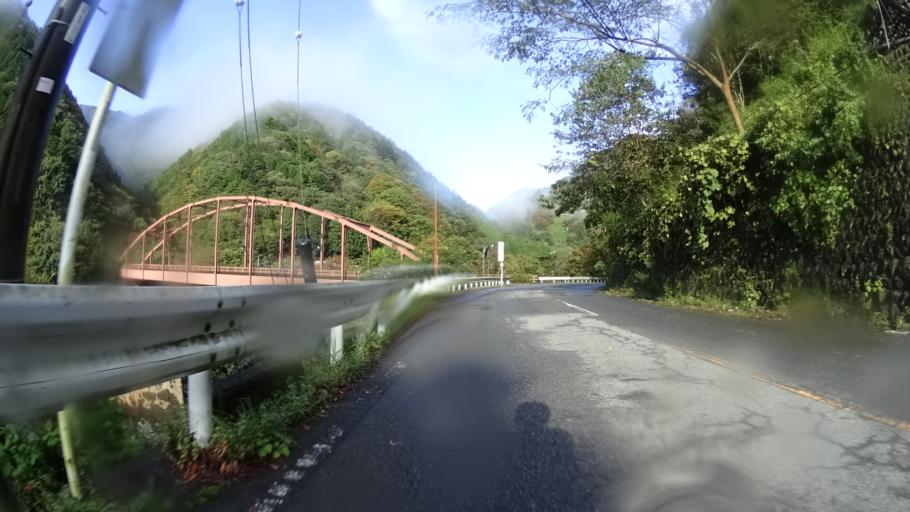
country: JP
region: Yamanashi
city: Otsuki
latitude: 35.7795
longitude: 138.9800
